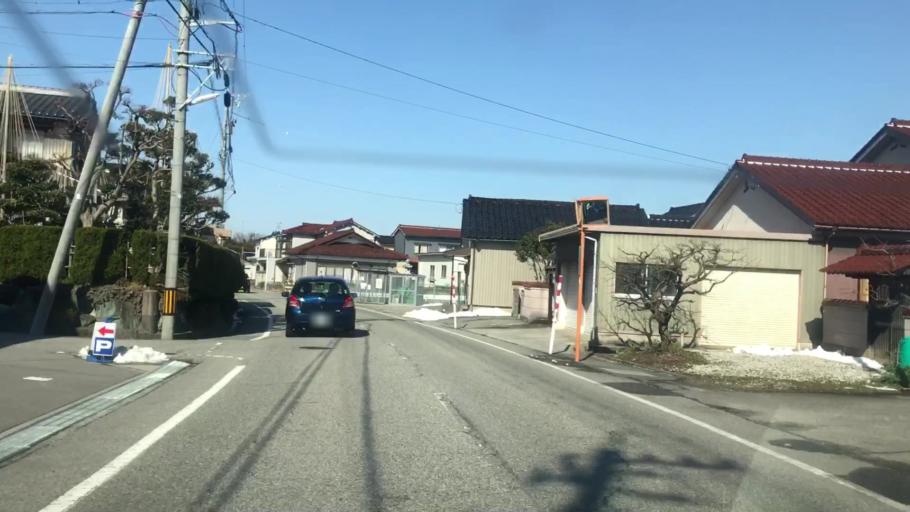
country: JP
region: Toyama
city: Toyama-shi
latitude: 36.6658
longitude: 137.2400
